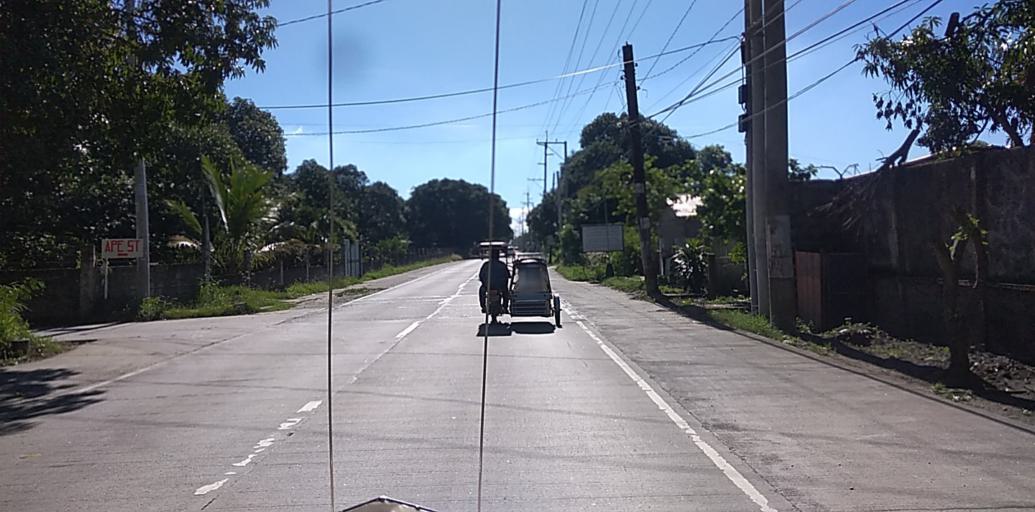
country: PH
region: Central Luzon
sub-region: Province of Pampanga
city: Santo Domingo
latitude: 15.0654
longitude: 120.7682
